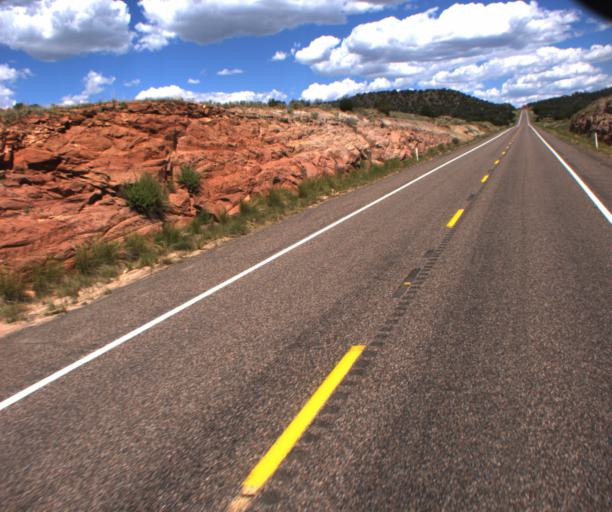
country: US
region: Arizona
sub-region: Apache County
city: Springerville
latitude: 34.1622
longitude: -109.0740
